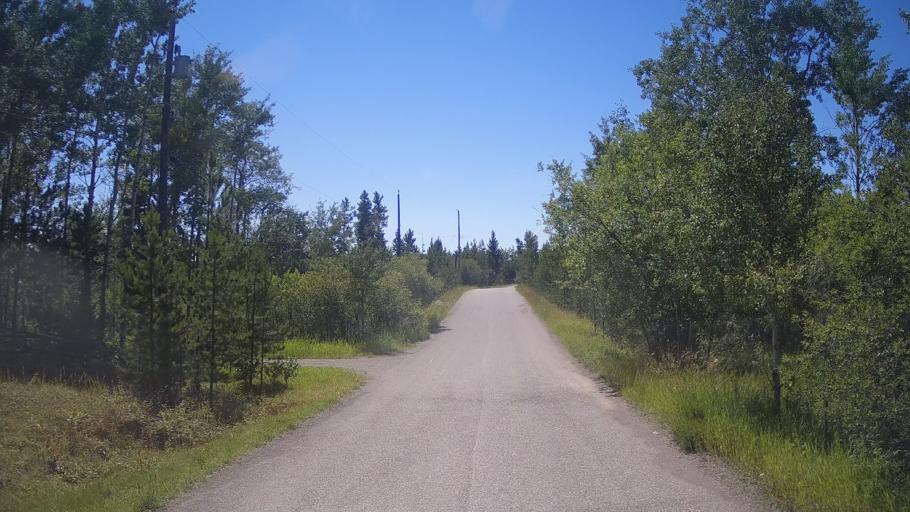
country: CA
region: British Columbia
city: Cache Creek
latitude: 51.3166
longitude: -121.3927
